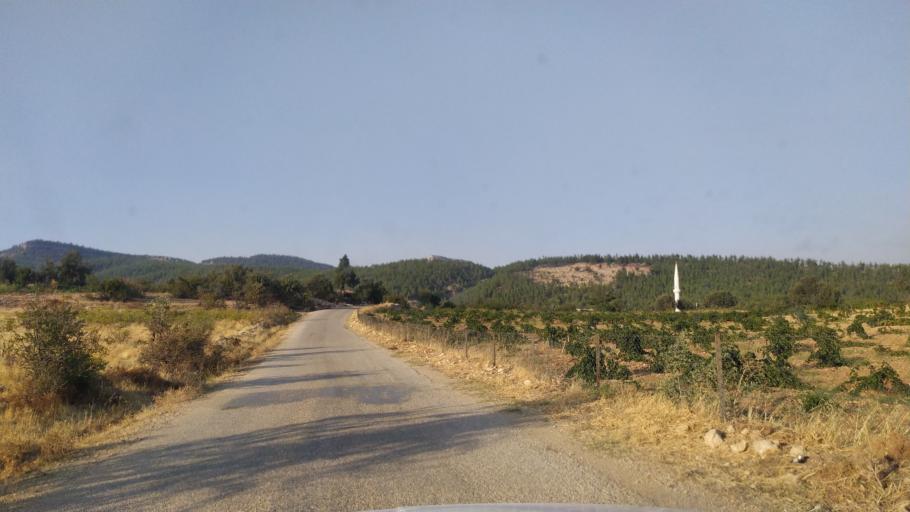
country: TR
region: Mersin
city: Mut
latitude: 36.6907
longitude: 33.1985
